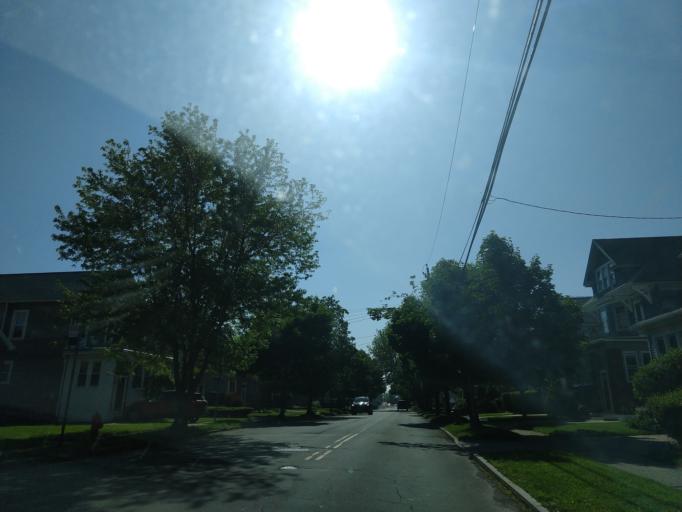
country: US
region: New York
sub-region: Erie County
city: West Seneca
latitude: 42.8469
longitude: -78.8204
